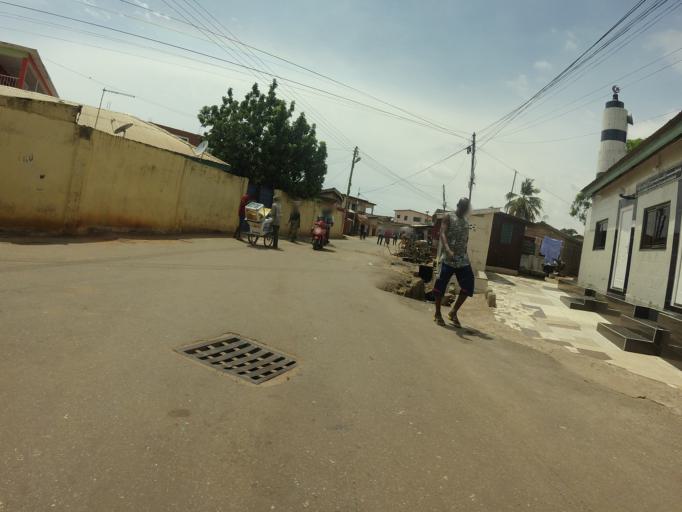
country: GH
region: Greater Accra
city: Accra
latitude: 5.5892
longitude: -0.2060
